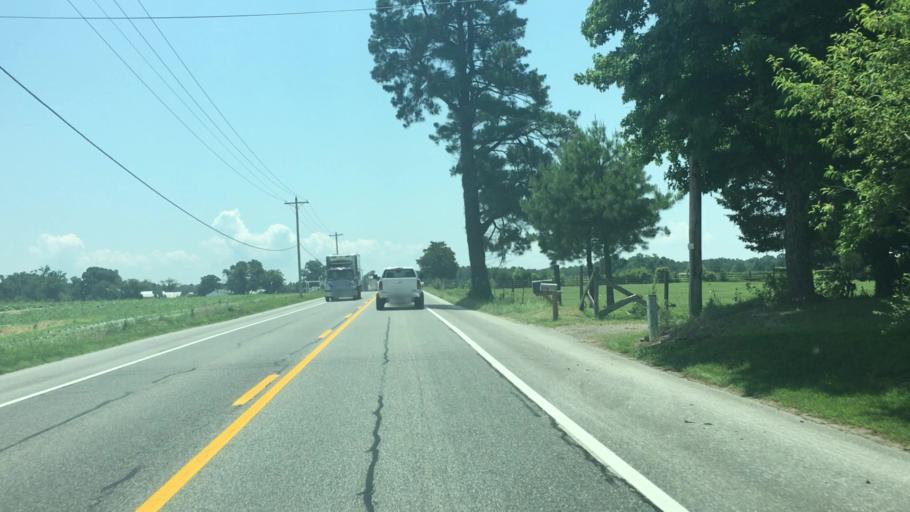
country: US
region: Maryland
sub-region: Saint Mary's County
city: Mechanicsville
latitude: 38.3797
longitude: -76.6774
